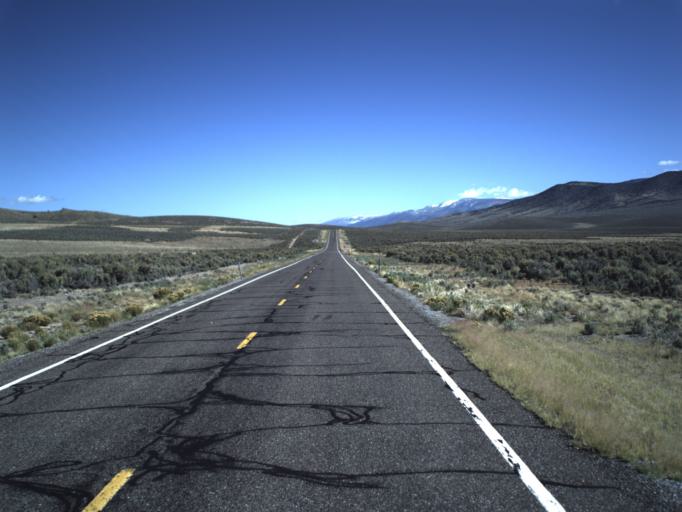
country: US
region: Utah
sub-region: Piute County
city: Junction
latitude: 38.2914
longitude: -111.9763
